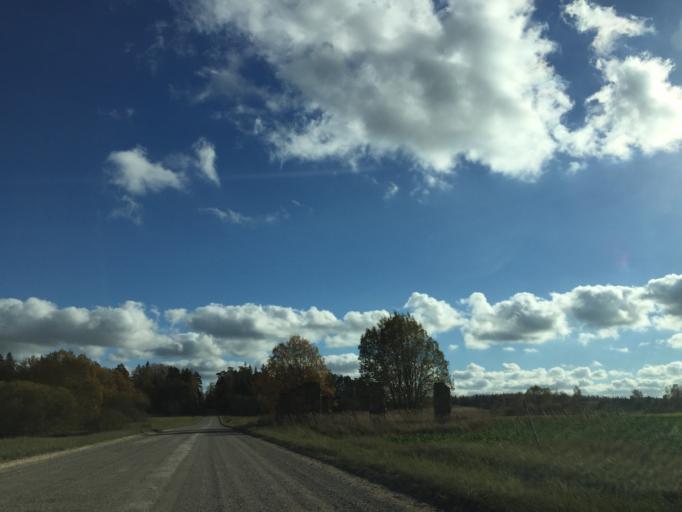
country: LV
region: Tukuma Rajons
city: Tukums
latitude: 56.9656
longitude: 22.9683
